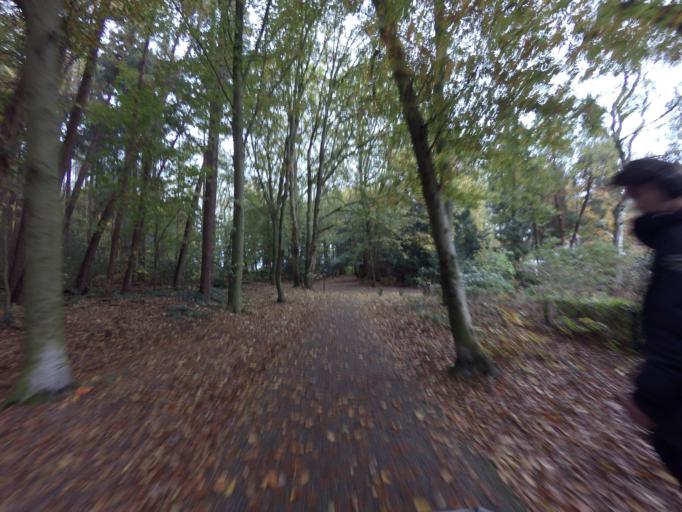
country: NL
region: North Holland
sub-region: Gemeente Hilversum
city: Hilversum
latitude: 52.2062
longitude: 5.1769
